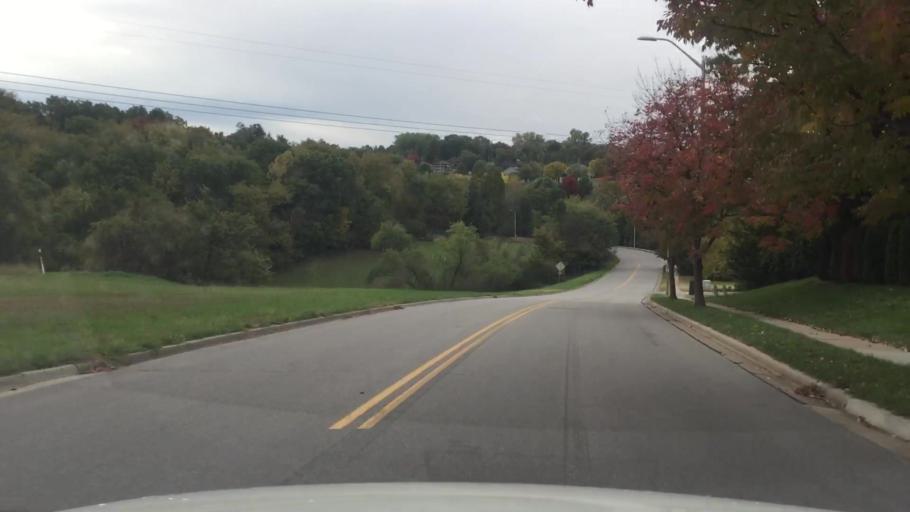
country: US
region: Kansas
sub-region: Johnson County
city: Shawnee
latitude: 39.0271
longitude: -94.7444
